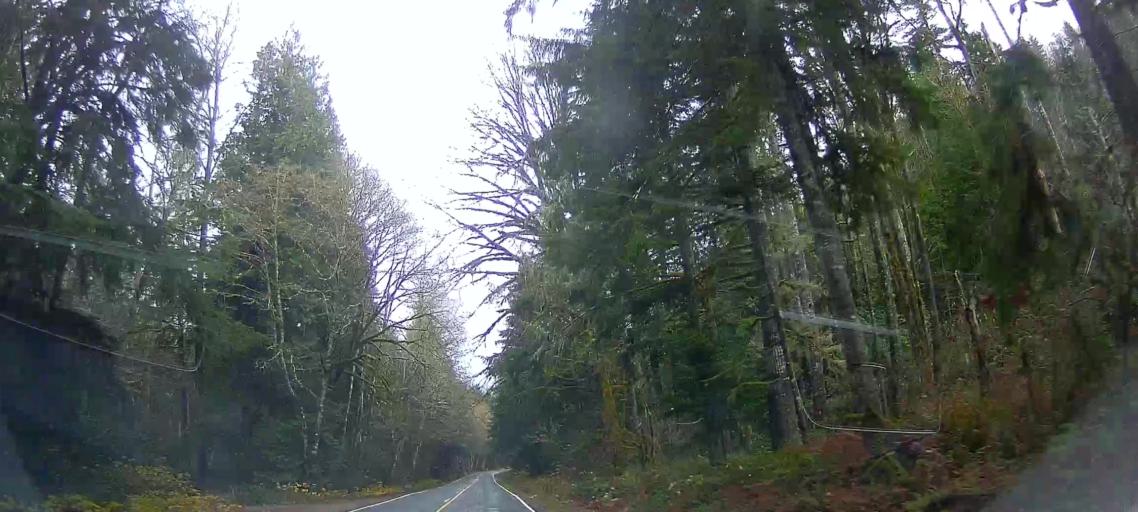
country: US
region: Washington
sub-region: Snohomish County
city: Darrington
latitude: 48.4839
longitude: -121.4956
